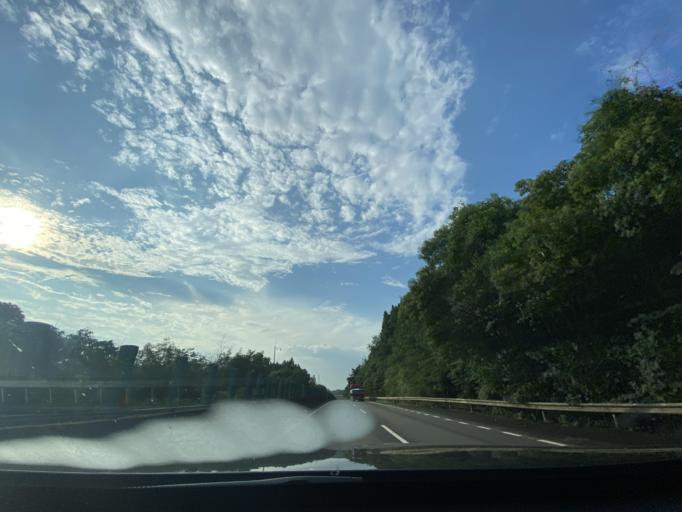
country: CN
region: Sichuan
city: Jiancheng
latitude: 30.3164
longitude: 104.5760
